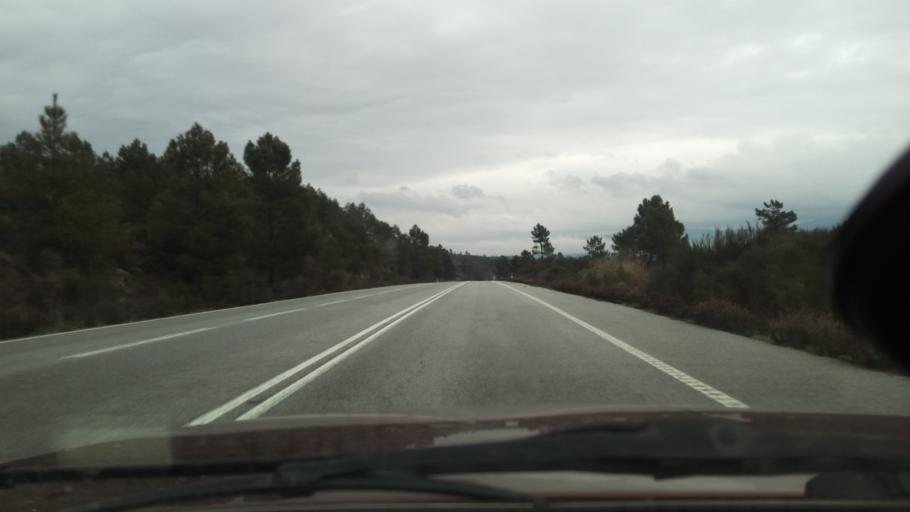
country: PT
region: Guarda
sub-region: Fornos de Algodres
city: Fornos de Algodres
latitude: 40.6034
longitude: -7.5689
